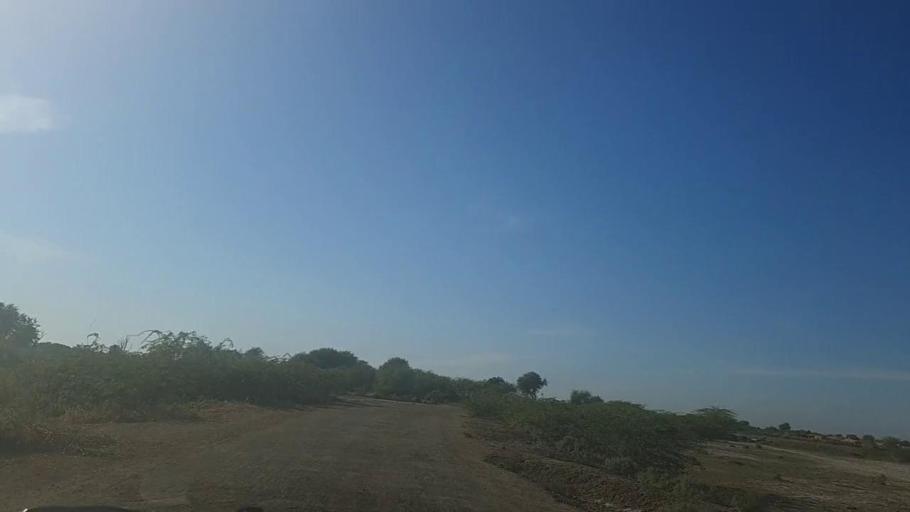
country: PK
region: Sindh
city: Pithoro
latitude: 25.5115
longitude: 69.3889
